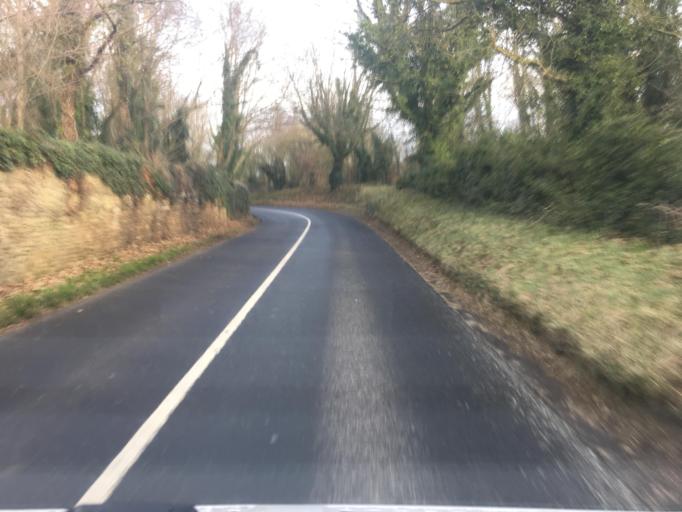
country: FR
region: Lower Normandy
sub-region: Departement du Calvados
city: Creully
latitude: 49.2902
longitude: -0.5417
